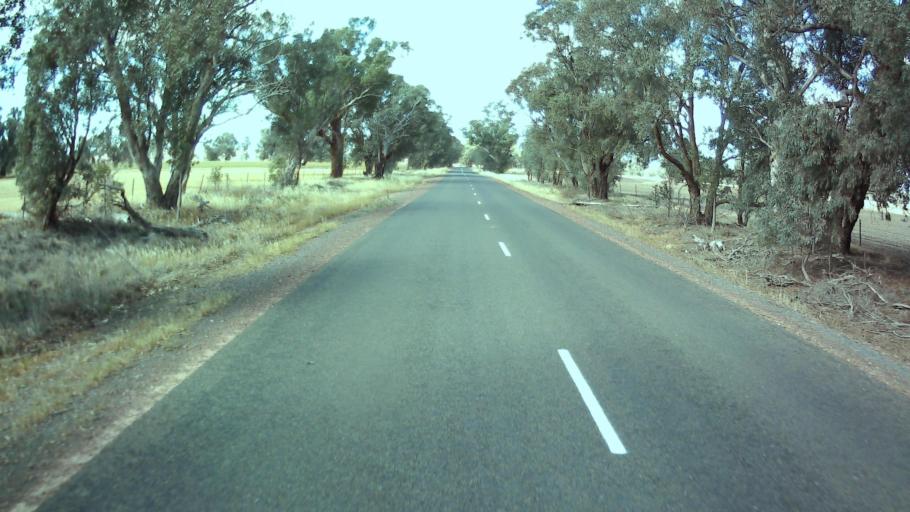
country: AU
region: New South Wales
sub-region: Weddin
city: Grenfell
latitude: -33.9815
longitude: 148.4180
